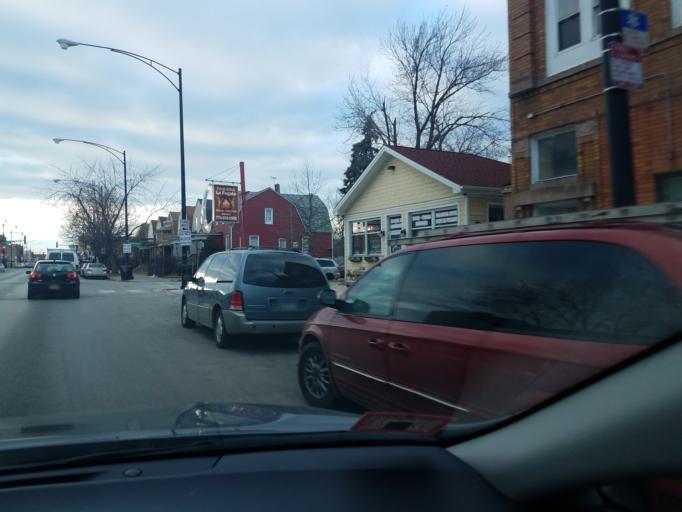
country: US
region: Illinois
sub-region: Cook County
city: Lincolnwood
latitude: 41.9610
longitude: -87.7262
